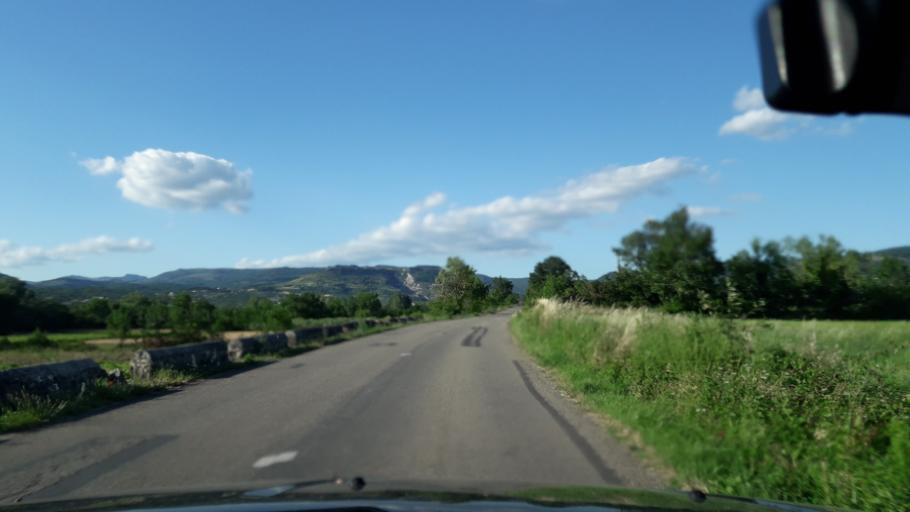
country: FR
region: Rhone-Alpes
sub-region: Departement de l'Ardeche
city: Lavilledieu
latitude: 44.5995
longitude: 4.4637
